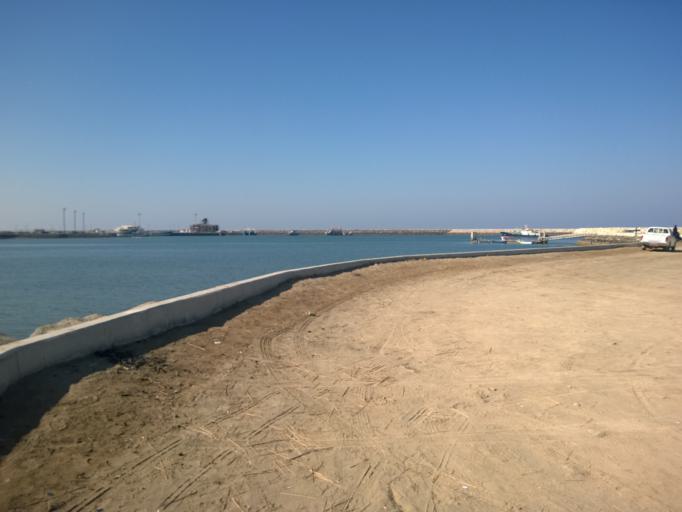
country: OM
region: Muhafazat Masqat
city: As Sib al Jadidah
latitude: 23.6871
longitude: 58.1831
